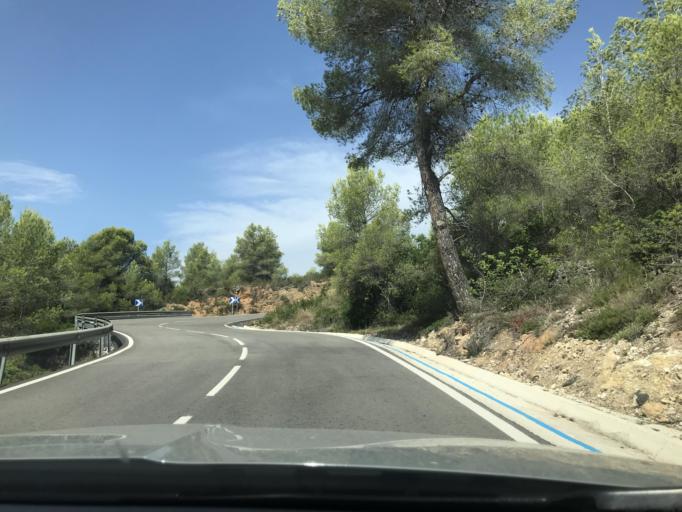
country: ES
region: Catalonia
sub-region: Provincia de Tarragona
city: Salomo
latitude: 41.1914
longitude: 1.3835
